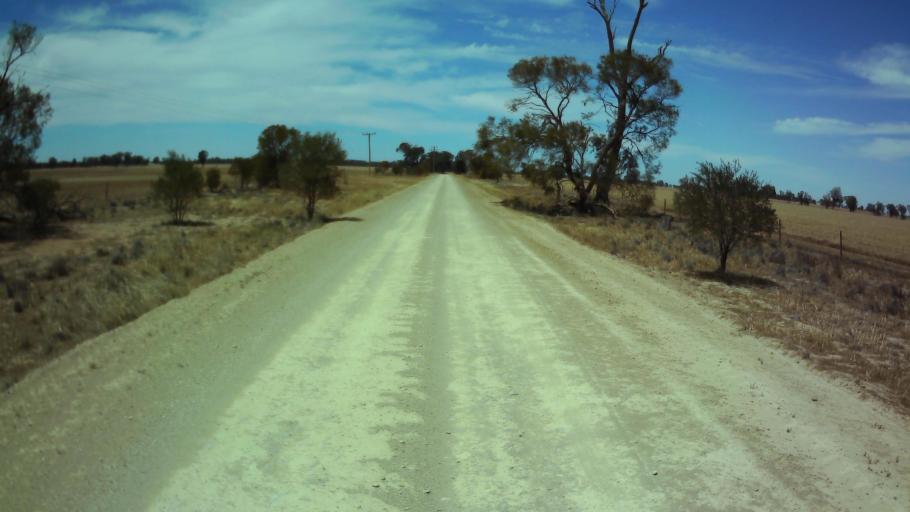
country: AU
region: New South Wales
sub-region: Weddin
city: Grenfell
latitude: -33.8819
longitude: 147.8043
